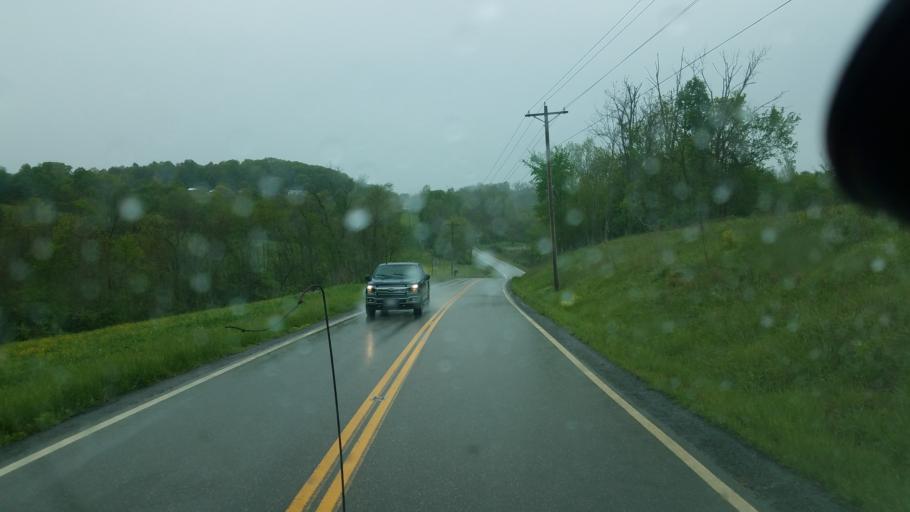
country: US
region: Ohio
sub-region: Muskingum County
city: Dresden
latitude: 40.2561
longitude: -82.0659
